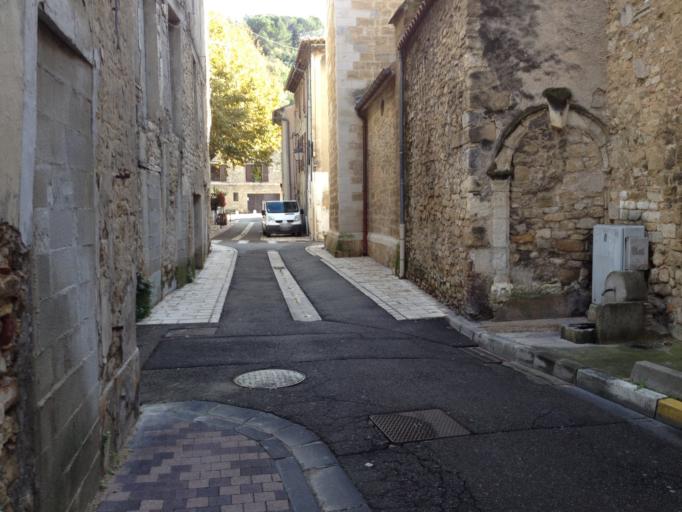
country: FR
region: Provence-Alpes-Cote d'Azur
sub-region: Departement du Vaucluse
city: Orange
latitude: 44.1360
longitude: 4.8062
